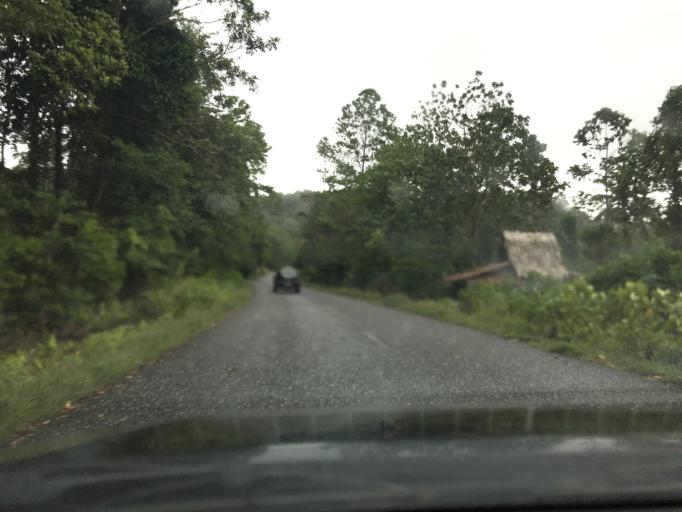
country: SB
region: Western Province
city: Gizo
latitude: -8.3140
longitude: 157.2540
